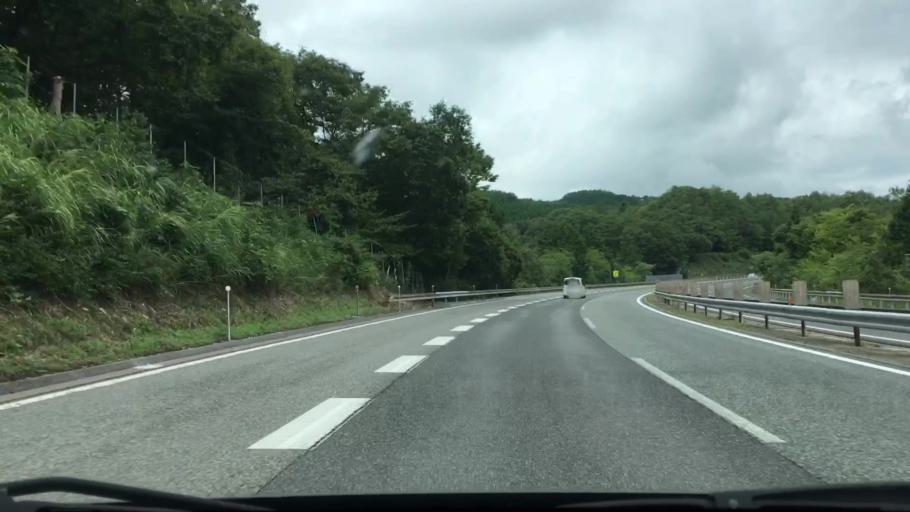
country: JP
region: Hiroshima
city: Miyoshi
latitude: 34.7528
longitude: 132.7651
